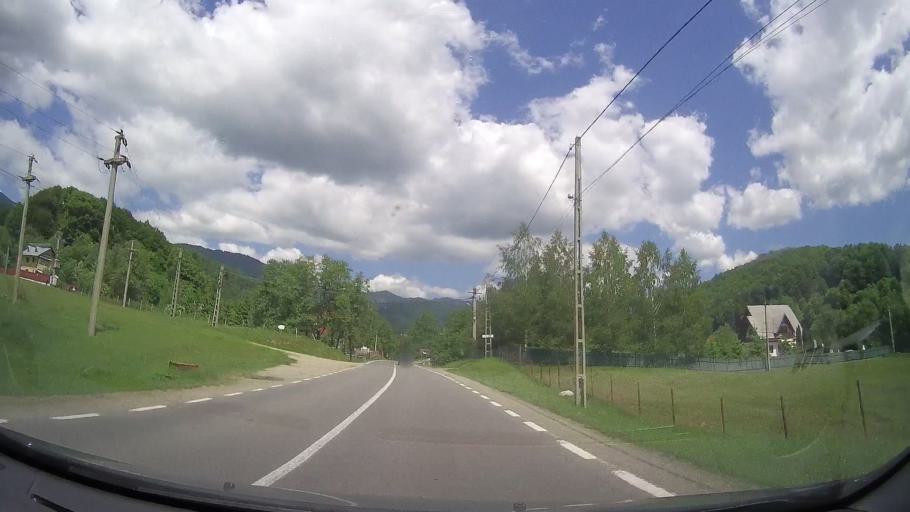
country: RO
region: Prahova
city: Maneciu
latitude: 45.4423
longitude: 25.9386
